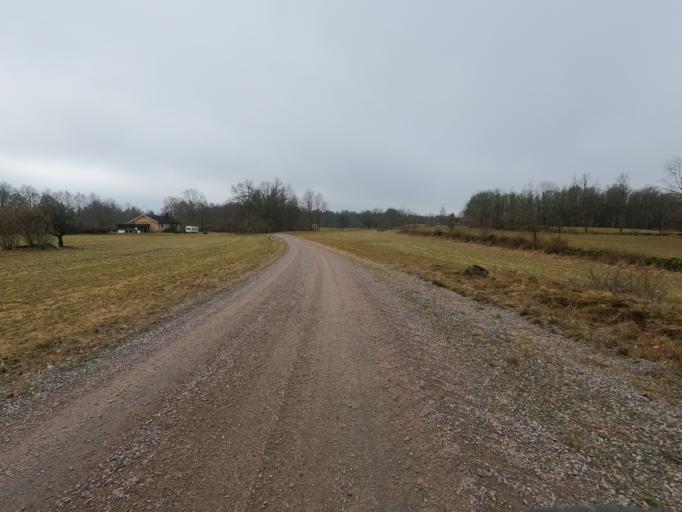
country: SE
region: Kronoberg
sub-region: Markaryds Kommun
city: Stromsnasbruk
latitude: 56.8242
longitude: 13.5634
